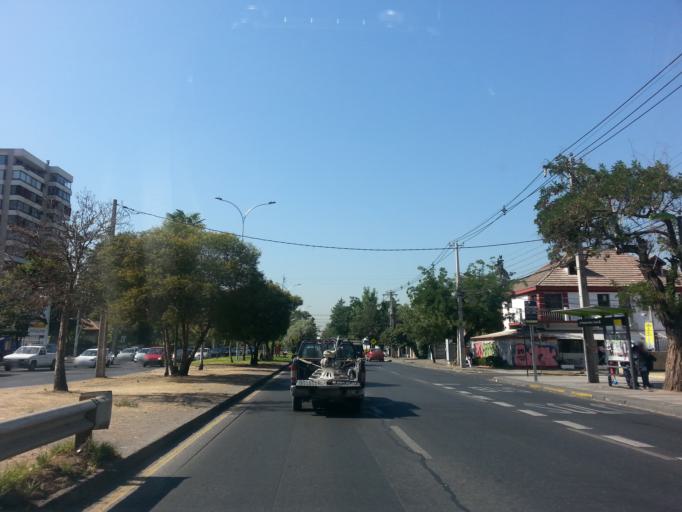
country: CL
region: Santiago Metropolitan
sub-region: Provincia de Santiago
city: Villa Presidente Frei, Nunoa, Santiago, Chile
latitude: -33.4388
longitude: -70.5734
